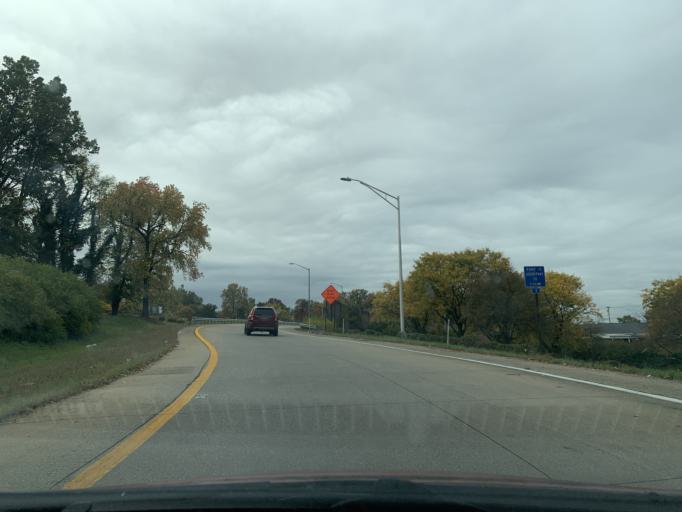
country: US
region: Kentucky
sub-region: Jefferson County
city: Audubon Park
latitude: 38.1910
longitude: -85.7672
